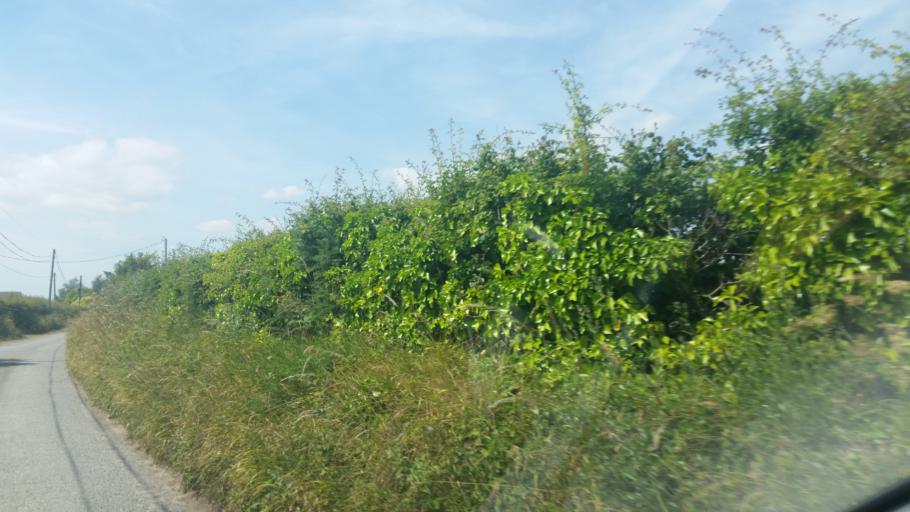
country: IE
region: Leinster
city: Lusk
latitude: 53.5351
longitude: -6.1578
